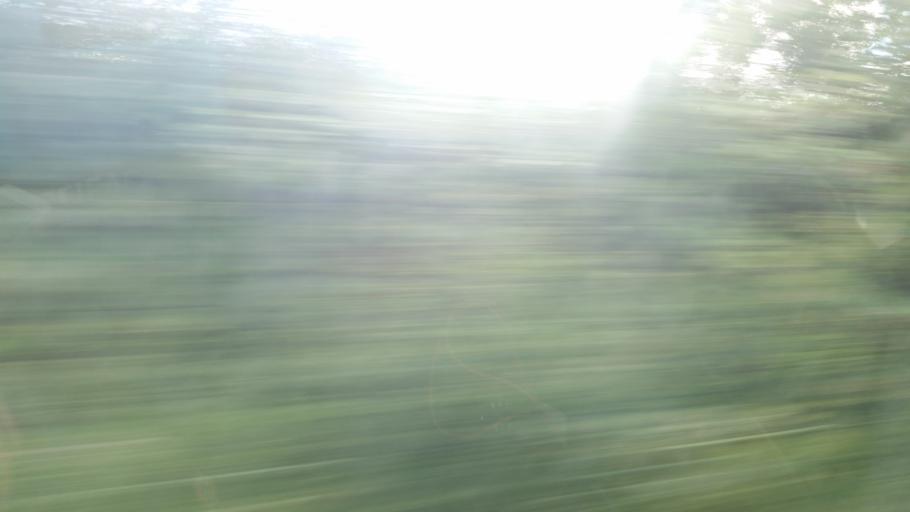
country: IE
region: Munster
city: Carrick-on-Suir
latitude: 52.3689
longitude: -7.4442
